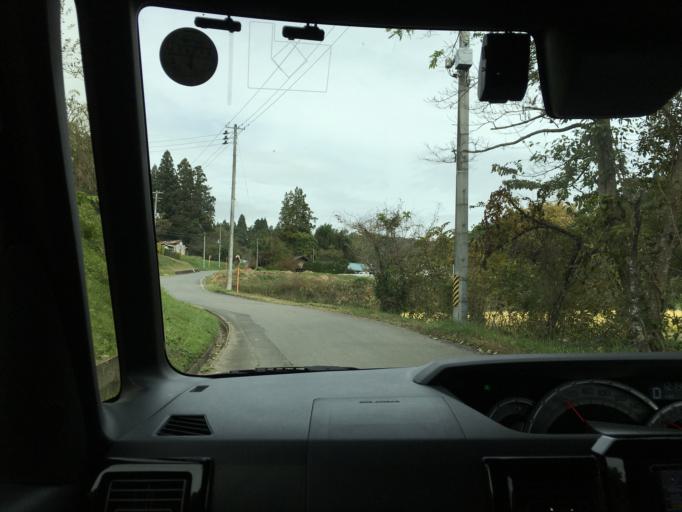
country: JP
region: Iwate
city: Ichinoseki
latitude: 39.0207
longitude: 141.3504
